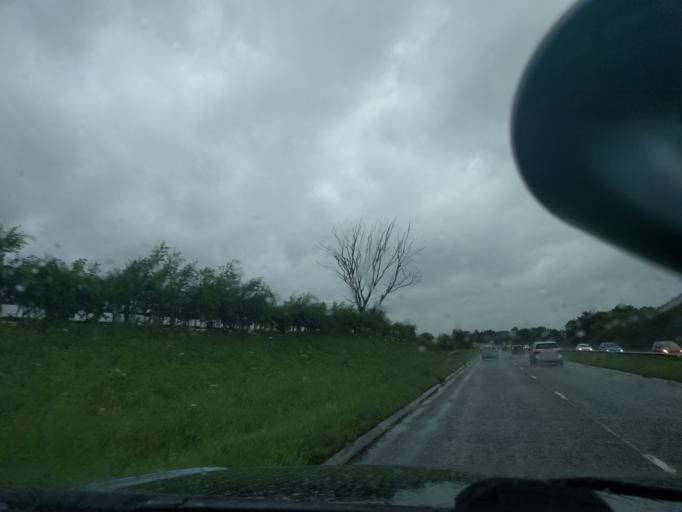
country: GB
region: England
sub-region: Wiltshire
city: Chippenham
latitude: 51.4952
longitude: -2.1266
